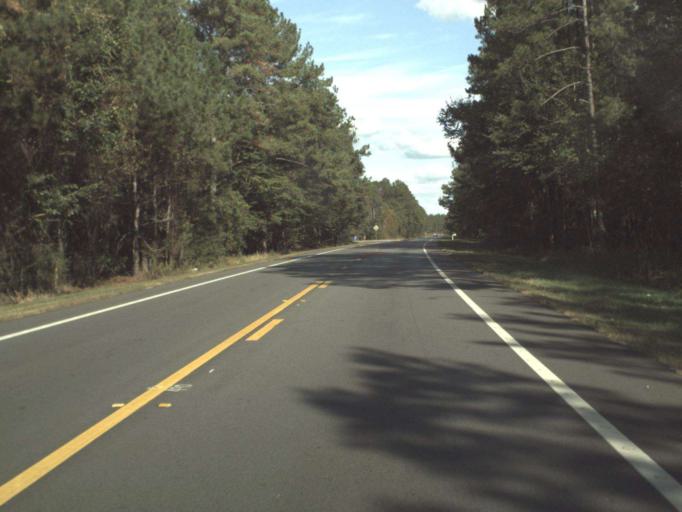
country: US
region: Florida
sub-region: Holmes County
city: Bonifay
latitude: 30.7775
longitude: -85.8017
